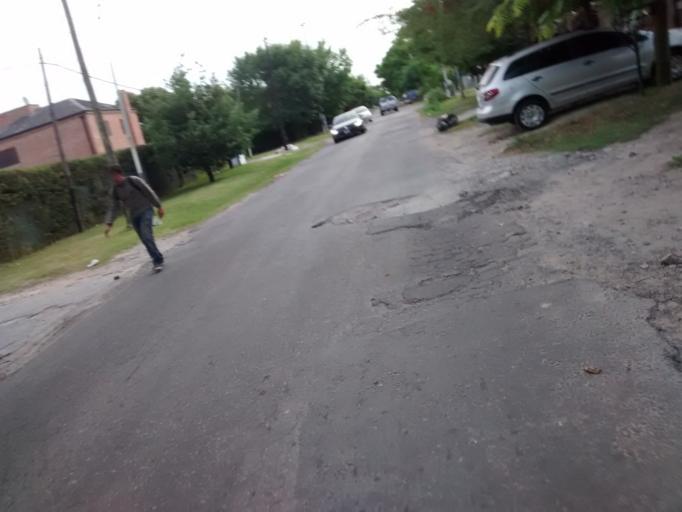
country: AR
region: Buenos Aires
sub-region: Partido de La Plata
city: La Plata
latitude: -34.8678
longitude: -58.0550
